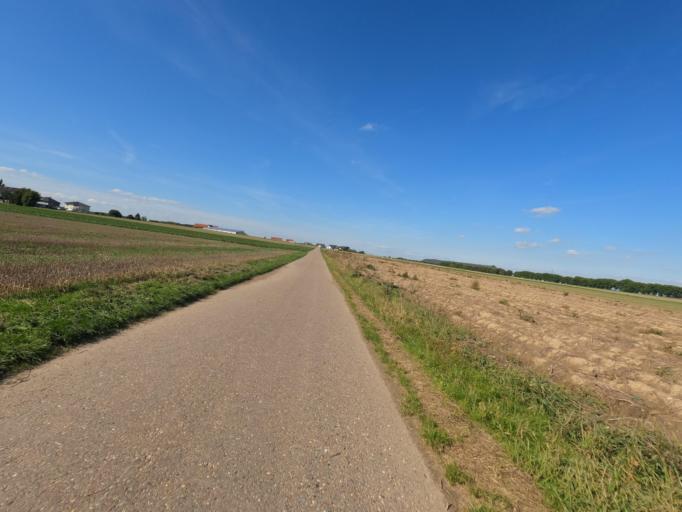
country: DE
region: North Rhine-Westphalia
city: Siersdorf
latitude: 50.8965
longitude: 6.2385
